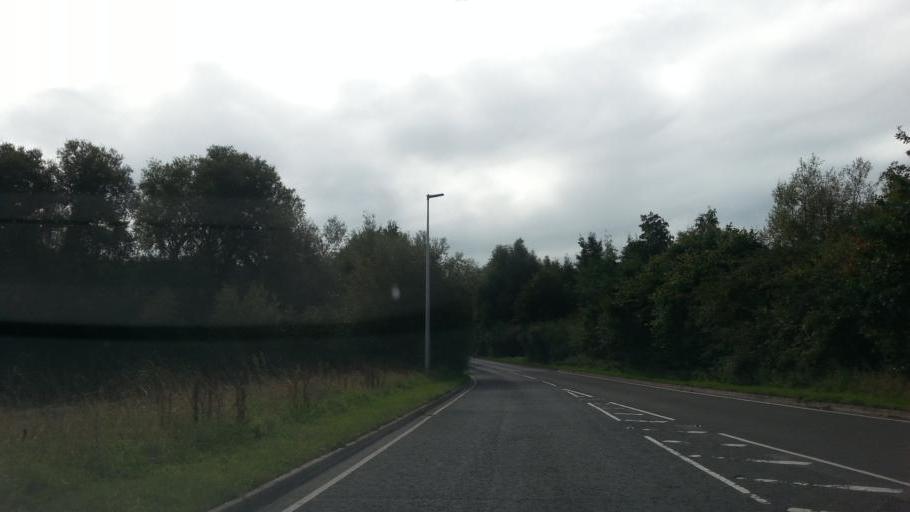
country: GB
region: England
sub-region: Herefordshire
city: Ross on Wye
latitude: 51.9203
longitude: -2.5706
